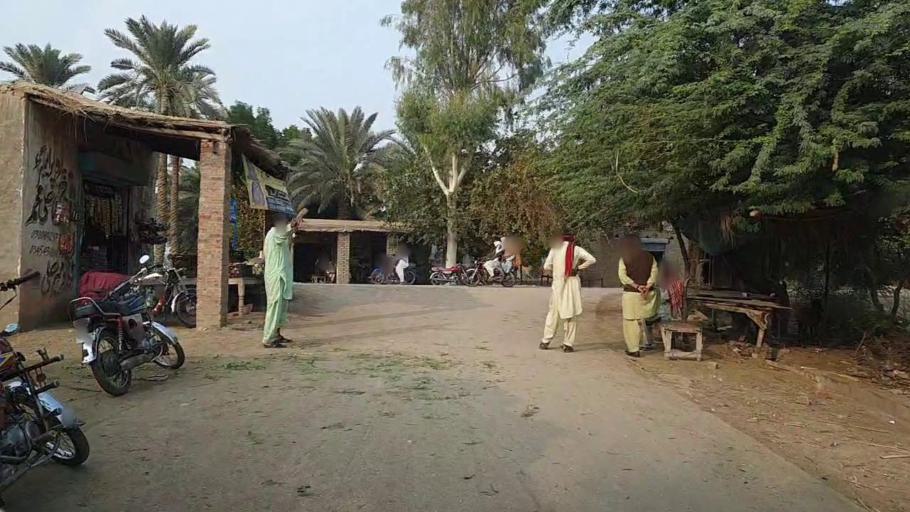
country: PK
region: Sindh
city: Setharja Old
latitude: 27.1008
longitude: 68.5055
